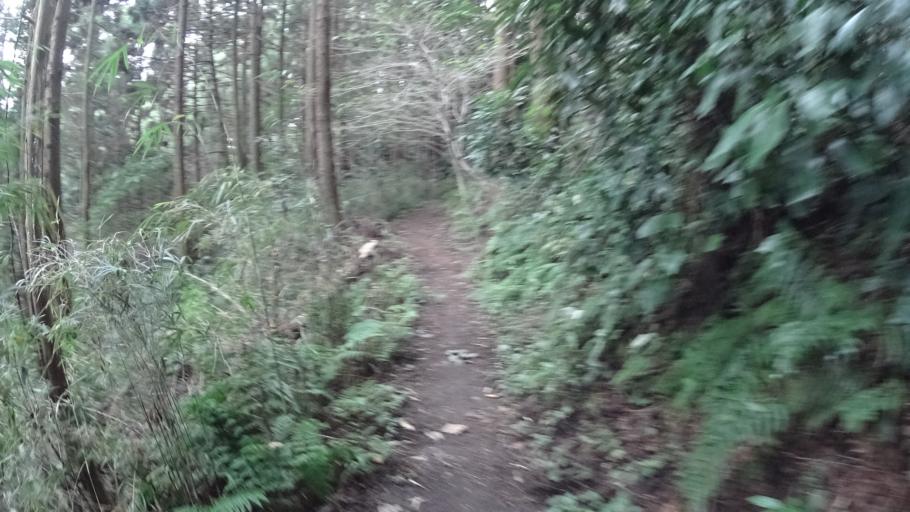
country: JP
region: Kanagawa
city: Zushi
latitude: 35.2857
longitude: 139.6211
